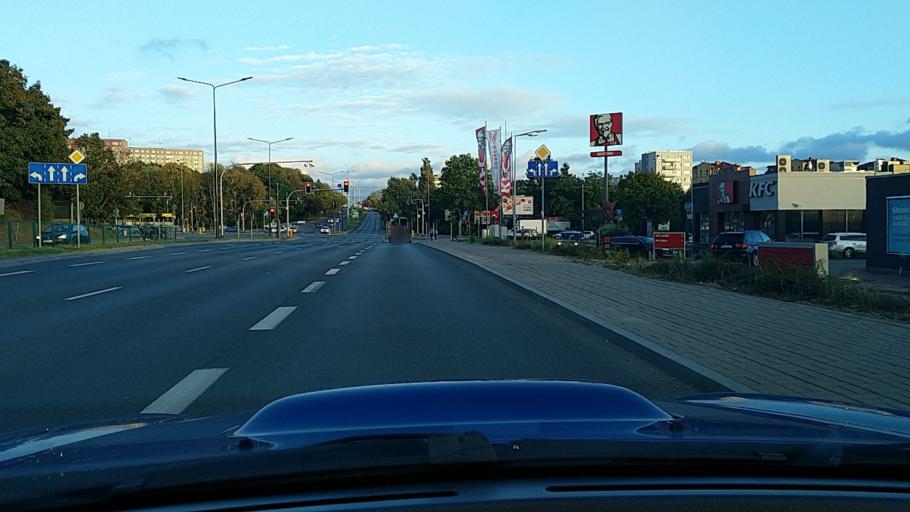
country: PL
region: Warmian-Masurian Voivodeship
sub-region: Powiat olsztynski
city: Olsztyn
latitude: 53.7667
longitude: 20.4861
